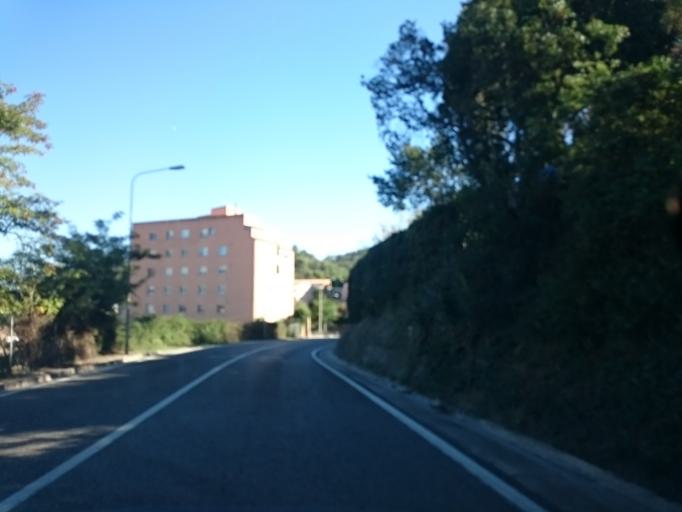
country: ES
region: Catalonia
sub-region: Provincia de Barcelona
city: Capellades
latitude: 41.5287
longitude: 1.6820
